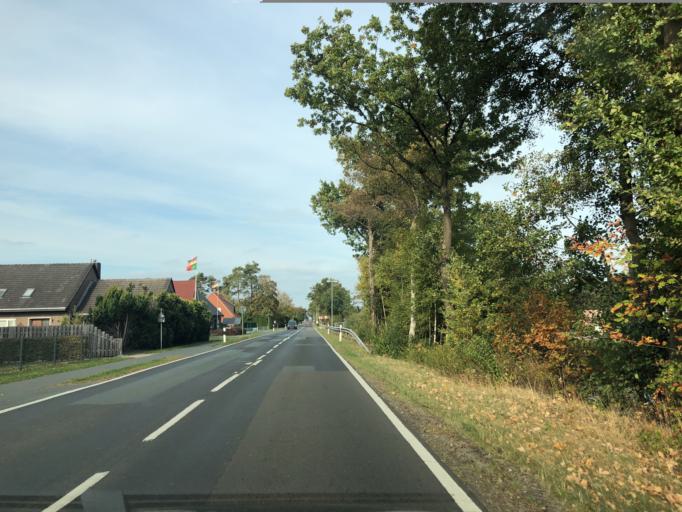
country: DE
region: Lower Saxony
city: Surwold
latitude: 53.0349
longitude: 7.4716
